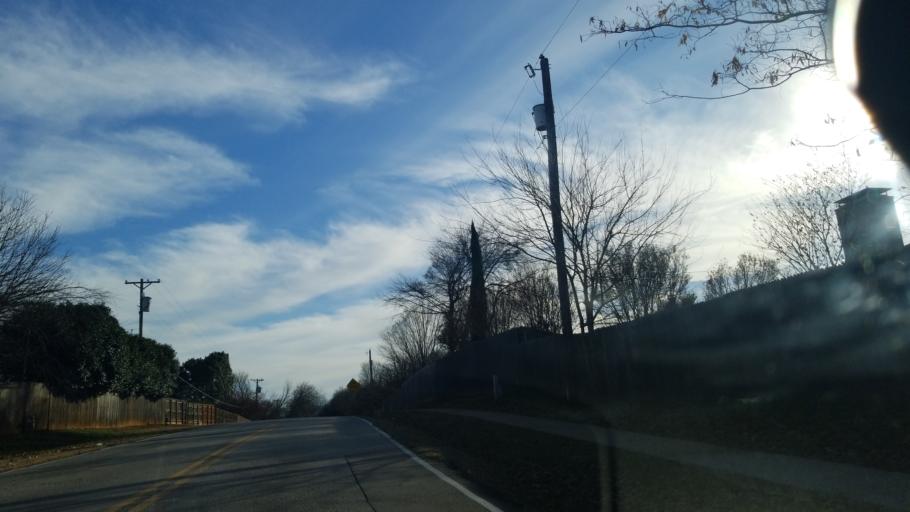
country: US
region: Texas
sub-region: Denton County
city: Corinth
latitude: 33.1385
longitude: -97.0559
